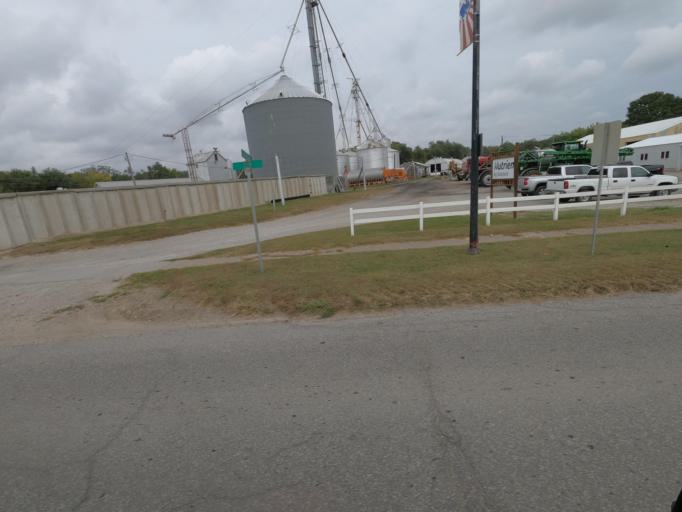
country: US
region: Iowa
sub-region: Wapello County
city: Ottumwa
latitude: 40.9176
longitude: -92.2213
